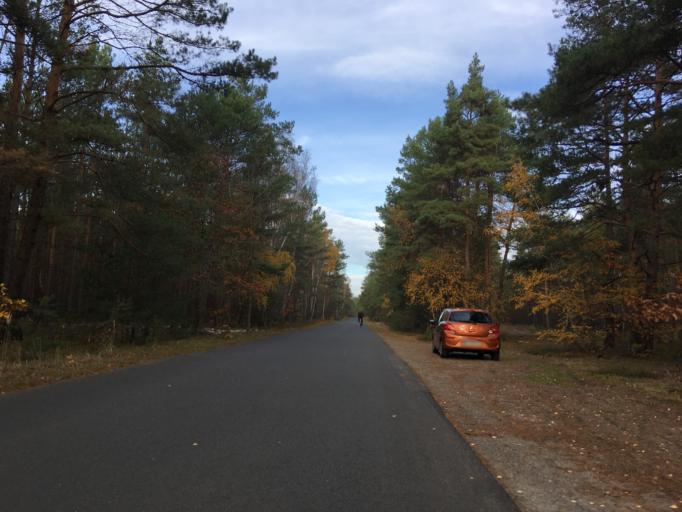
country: DE
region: Brandenburg
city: Halbe
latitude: 52.0829
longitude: 13.7783
